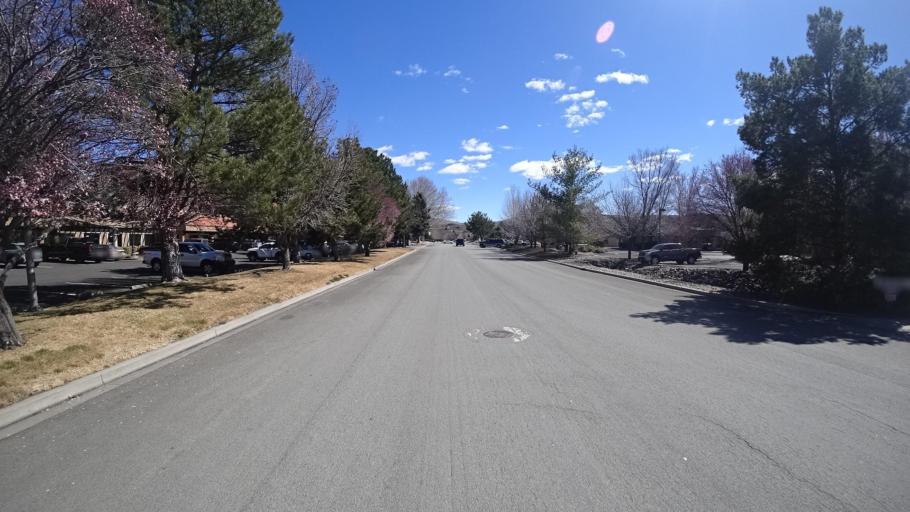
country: US
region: Nevada
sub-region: Washoe County
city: Sparks
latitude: 39.4723
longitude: -119.7683
